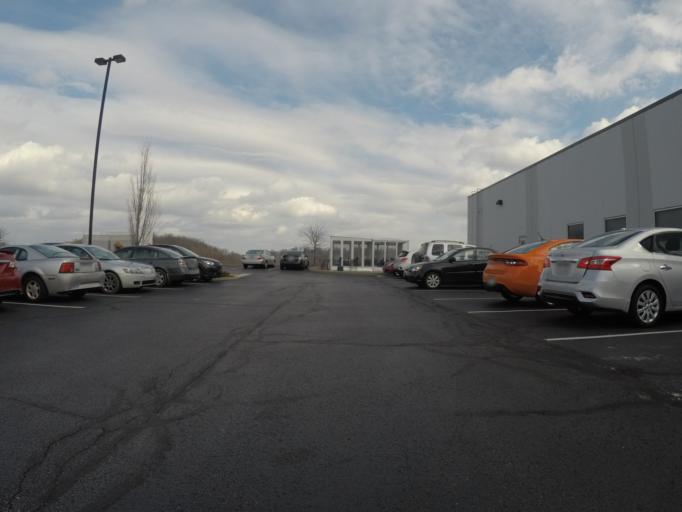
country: US
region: West Virginia
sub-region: Cabell County
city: Huntington
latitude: 38.3945
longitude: -82.4203
